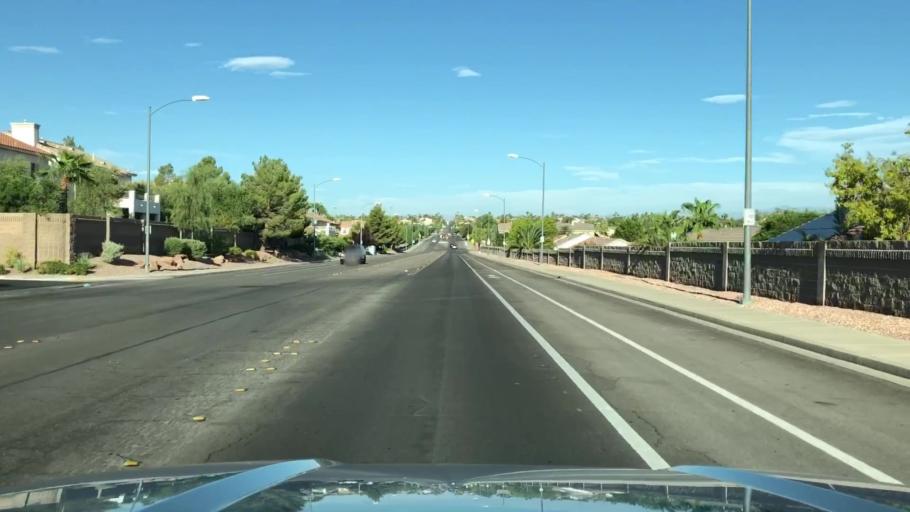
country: US
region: Nevada
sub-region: Clark County
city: Whitney
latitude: 36.0490
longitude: -115.0479
